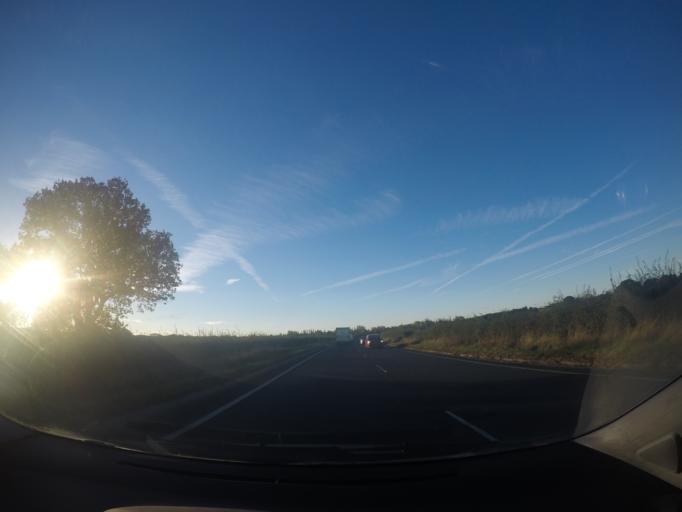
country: GB
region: England
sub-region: City of York
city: Copmanthorpe
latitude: 53.9304
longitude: -1.1440
